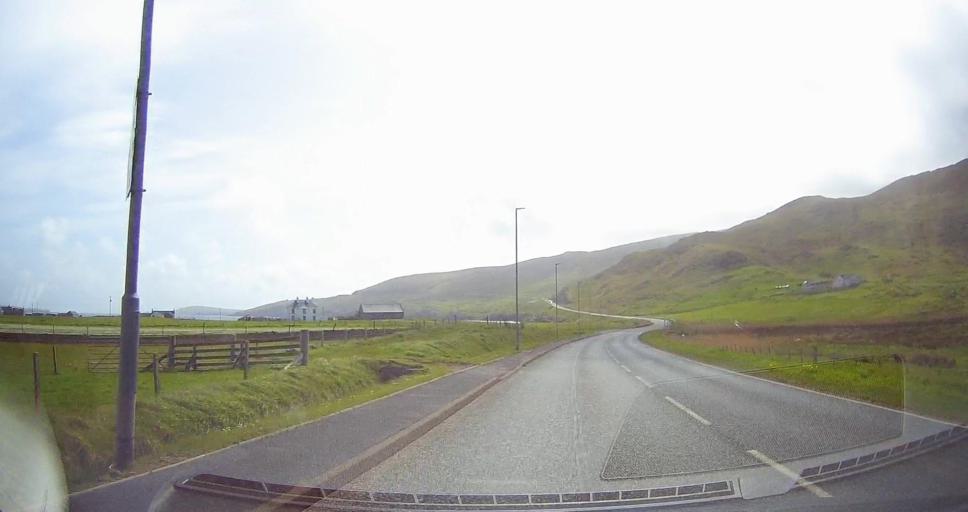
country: GB
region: Scotland
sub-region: Shetland Islands
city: Sandwick
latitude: 60.0374
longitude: -1.2299
